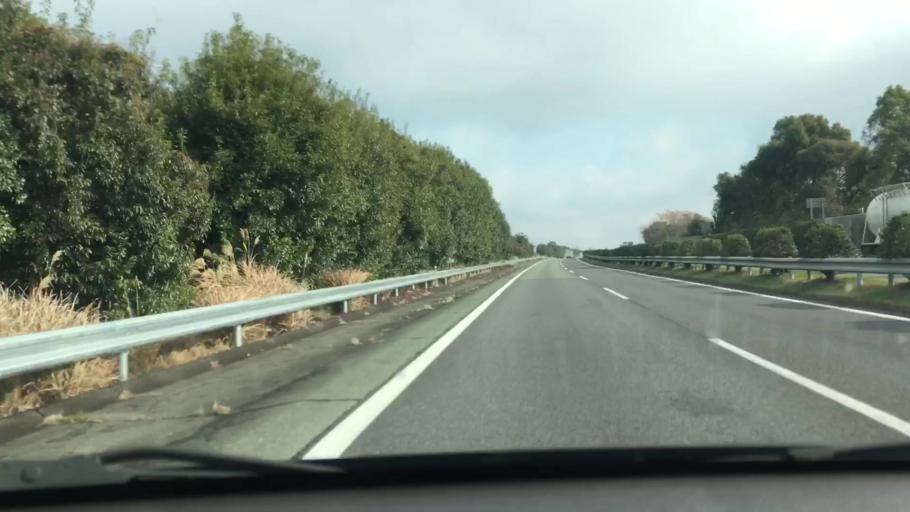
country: JP
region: Kumamoto
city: Kumamoto
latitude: 32.8554
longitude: 130.7568
